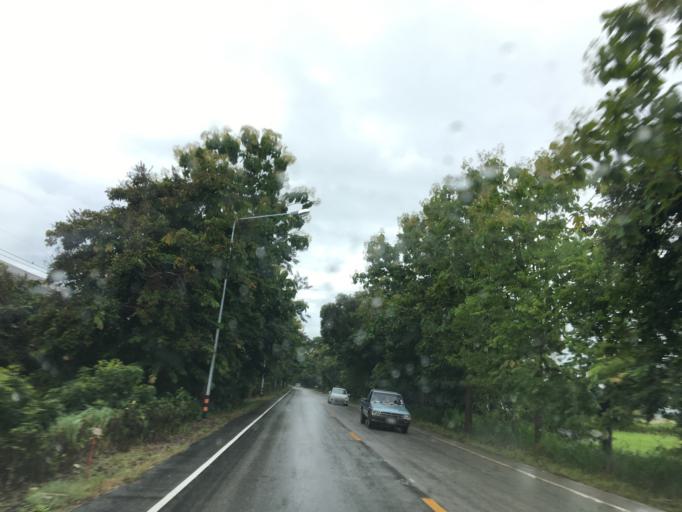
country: TH
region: Chiang Rai
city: Pa Daet
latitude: 19.5418
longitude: 99.9787
